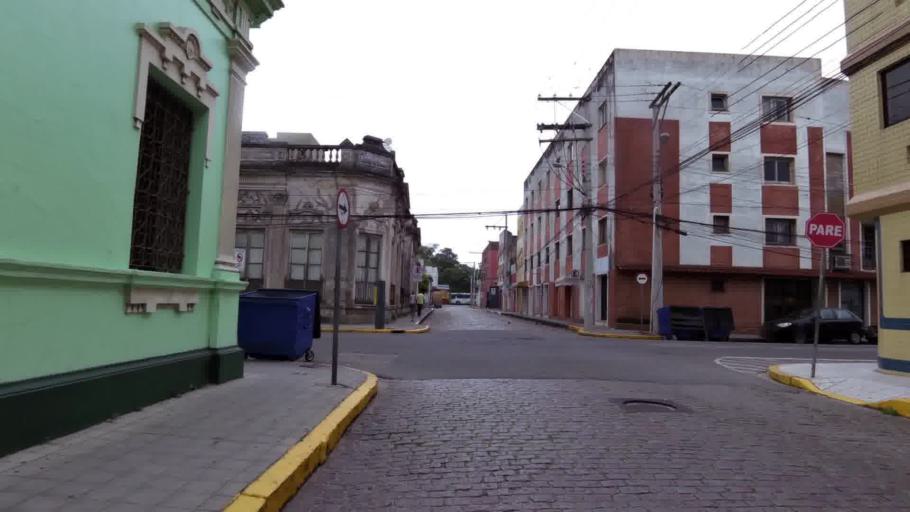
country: BR
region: Rio Grande do Sul
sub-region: Rio Grande
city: Rio Grande
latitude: -32.0308
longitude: -52.0991
